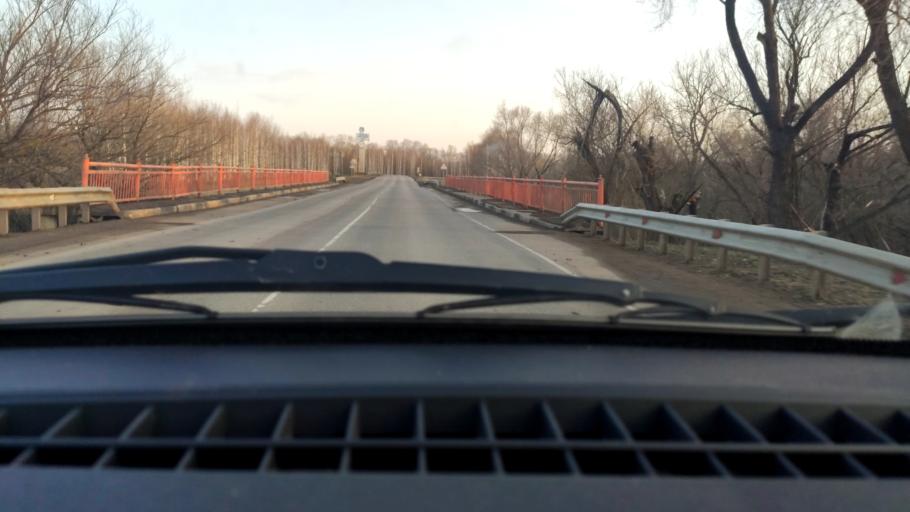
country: RU
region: Bashkortostan
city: Davlekanovo
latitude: 54.3660
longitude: 55.1953
